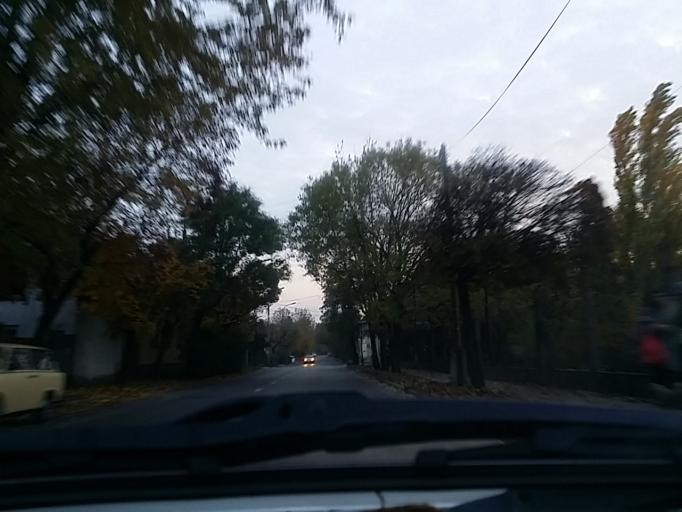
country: HU
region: Budapest
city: Budapest XV. keruelet
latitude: 47.5519
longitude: 19.1079
